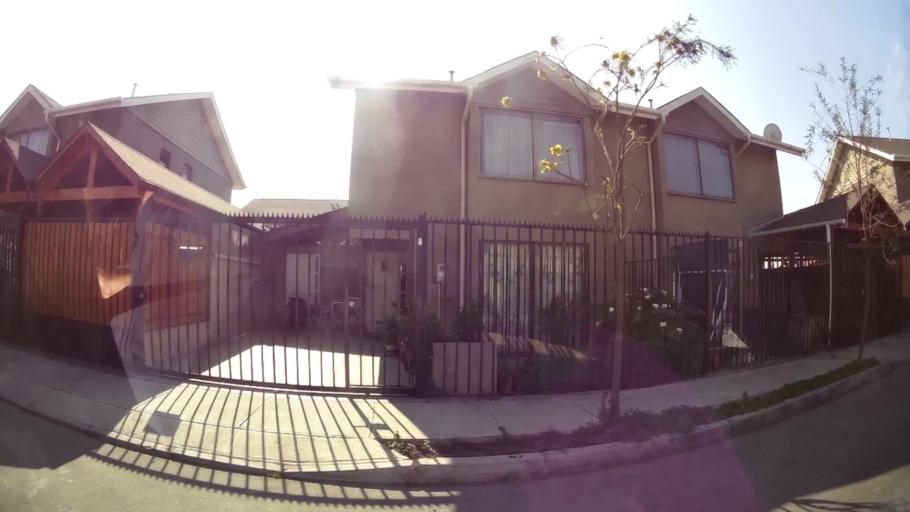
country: CL
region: Santiago Metropolitan
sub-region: Provincia de Santiago
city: Lo Prado
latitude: -33.4809
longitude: -70.7628
